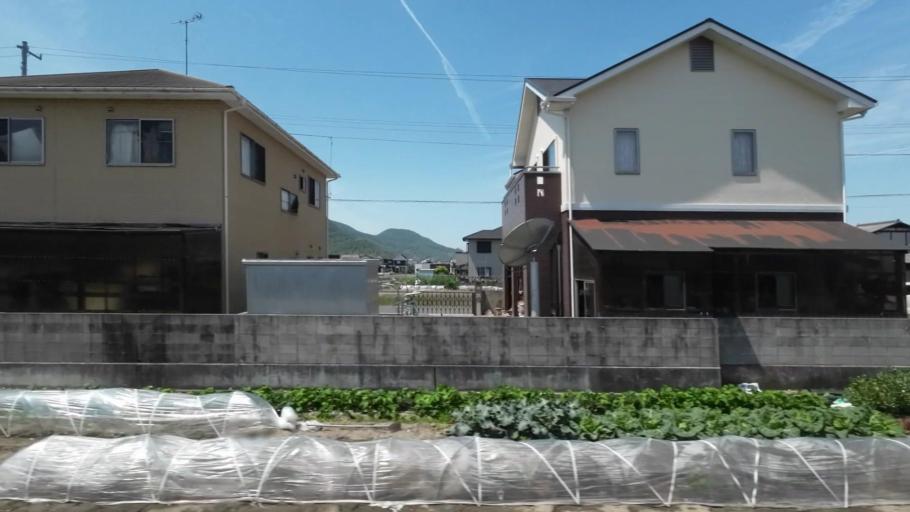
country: JP
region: Kagawa
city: Marugame
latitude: 34.2404
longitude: 133.7828
